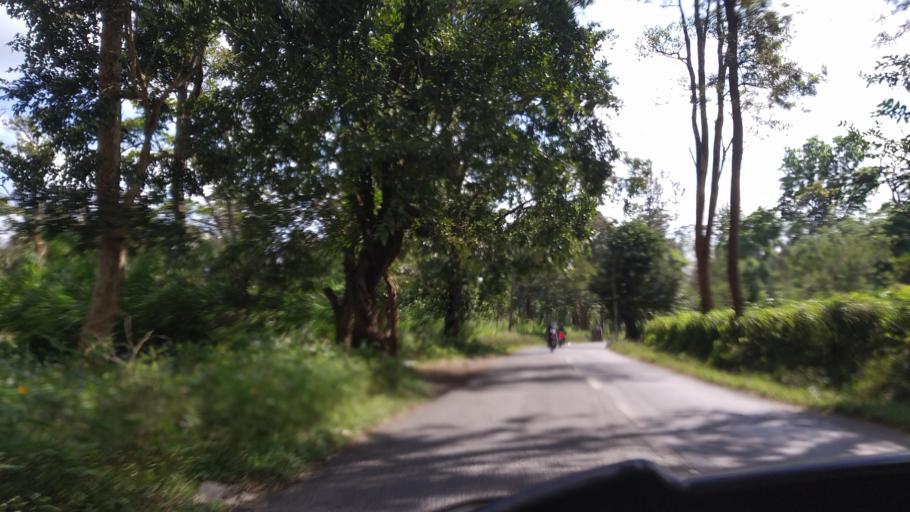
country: IN
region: Kerala
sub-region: Wayanad
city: Panamaram
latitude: 11.9517
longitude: 76.0652
